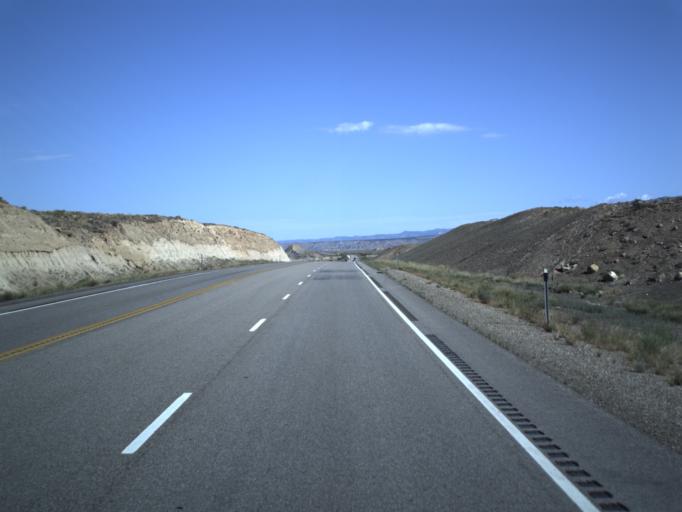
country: US
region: Utah
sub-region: Carbon County
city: East Carbon City
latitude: 39.2783
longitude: -110.3484
